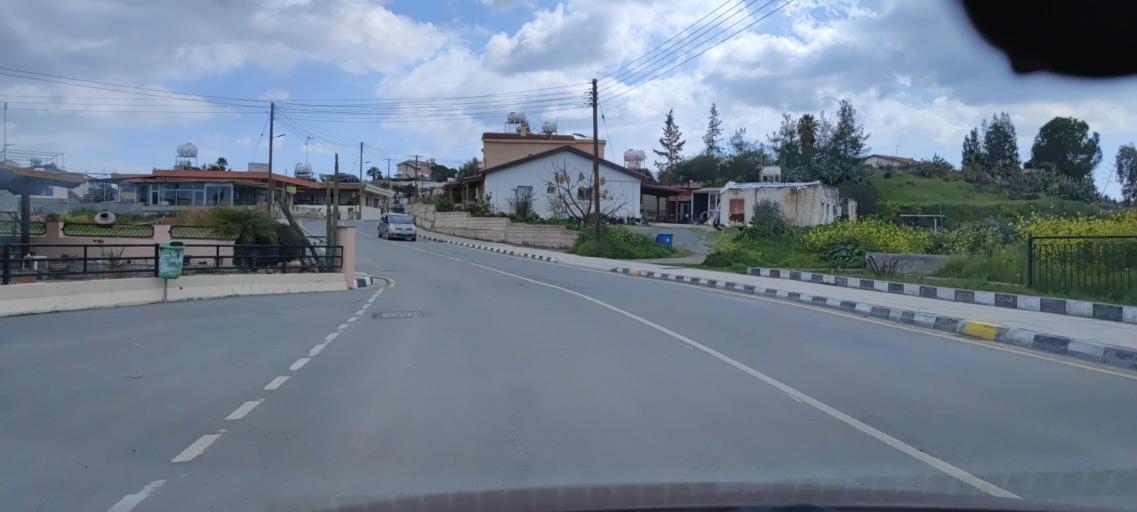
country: CY
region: Larnaka
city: Kornos
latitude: 34.9215
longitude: 33.3969
